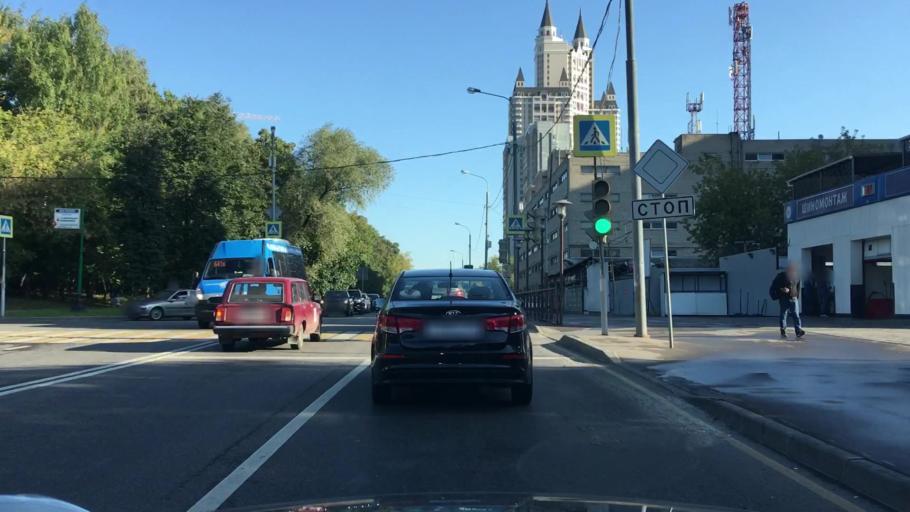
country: RU
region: Moscow
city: Davydkovo
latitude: 55.7227
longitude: 37.4788
